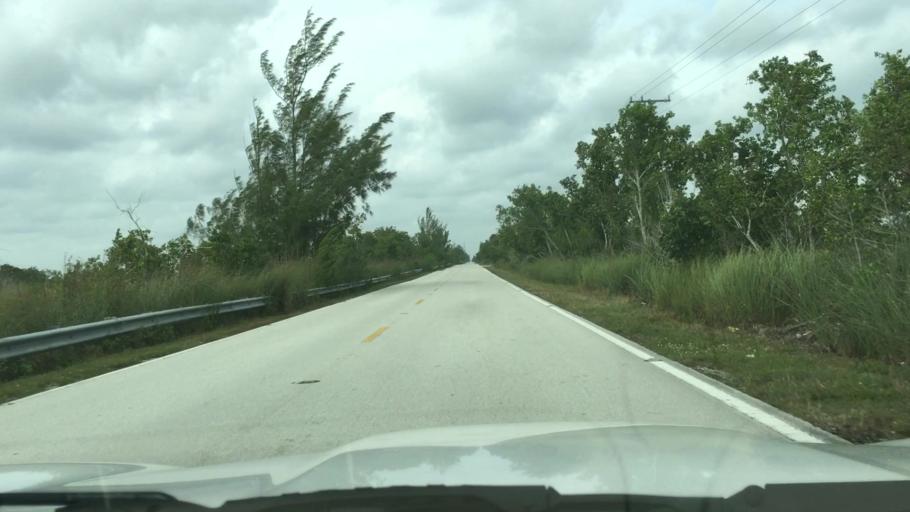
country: US
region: Florida
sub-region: Miami-Dade County
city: Florida City
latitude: 25.3512
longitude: -80.4195
